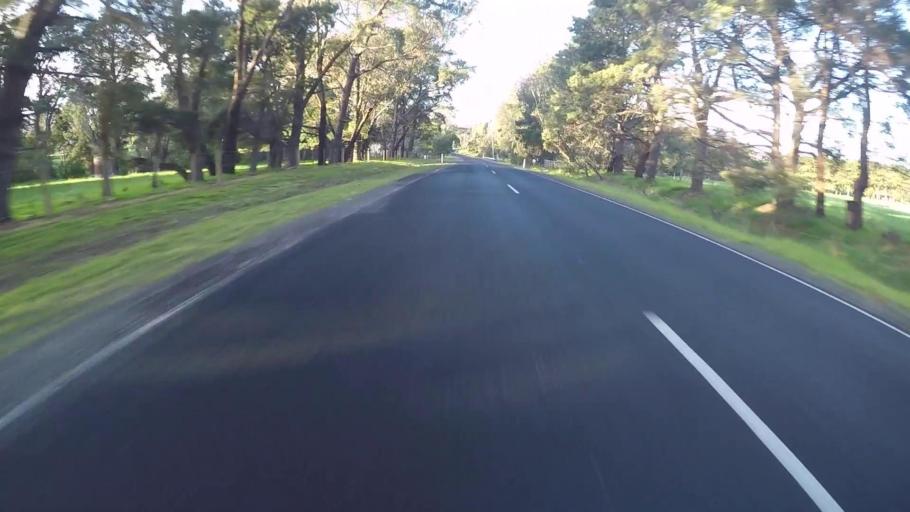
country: AU
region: Victoria
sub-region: Greater Geelong
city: Wandana Heights
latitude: -38.1481
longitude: 144.1800
